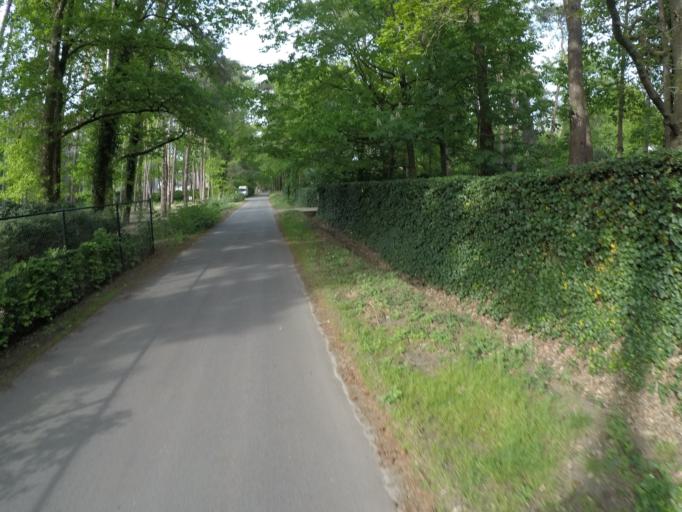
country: BE
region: Flanders
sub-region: Provincie Antwerpen
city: Kalmthout
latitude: 51.3461
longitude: 4.4701
